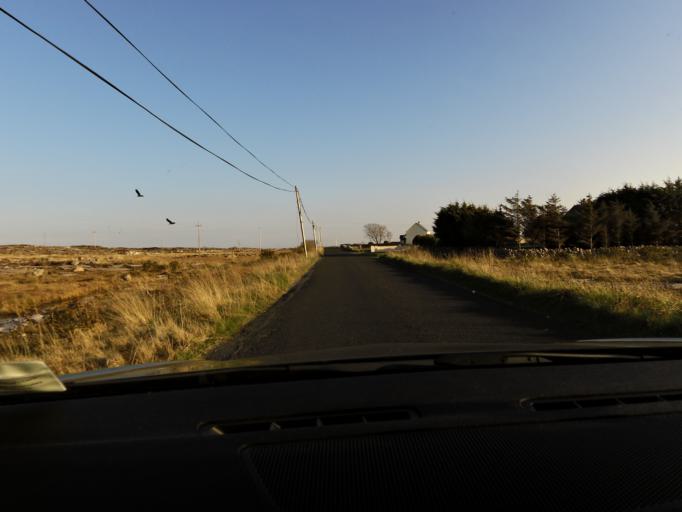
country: IE
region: Connaught
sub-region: County Galway
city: Oughterard
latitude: 53.2504
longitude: -9.5408
